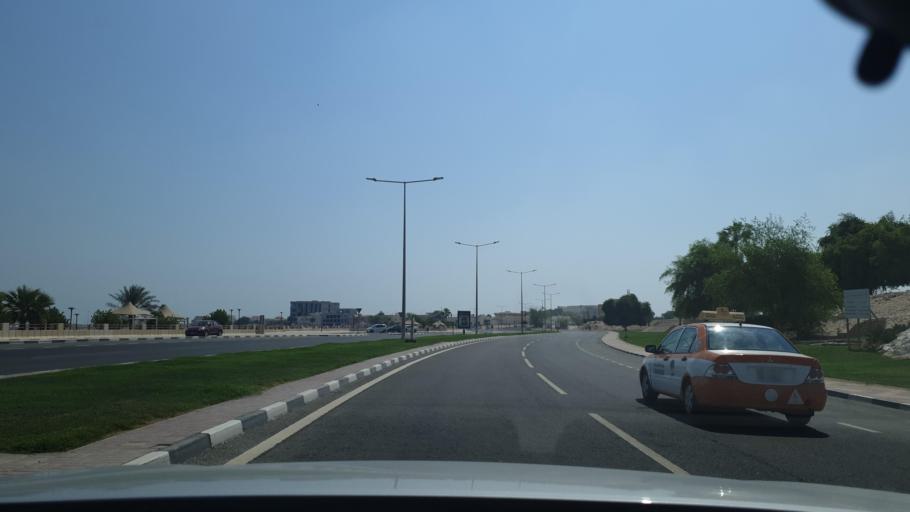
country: QA
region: Al Khawr
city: Al Khawr
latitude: 25.6887
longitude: 51.5064
